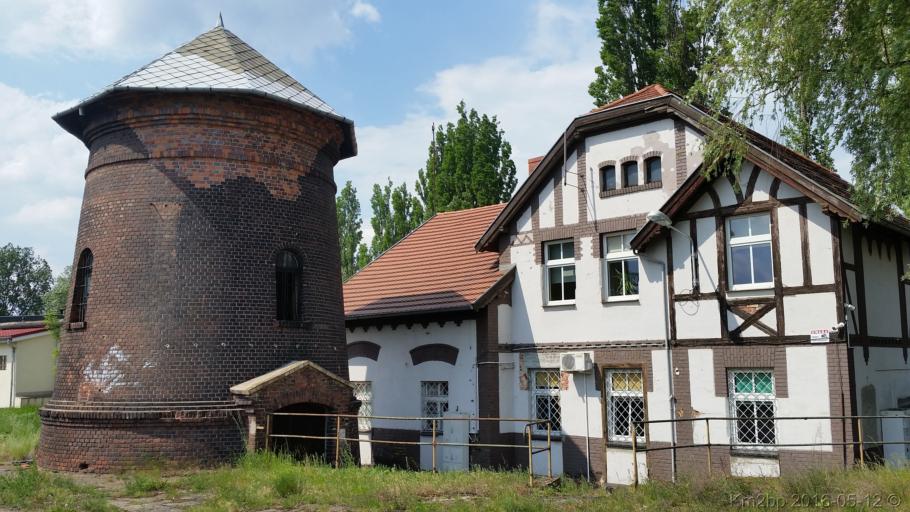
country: PL
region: Lubusz
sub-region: Zielona Gora
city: Zielona Gora
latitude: 51.9476
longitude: 15.5066
